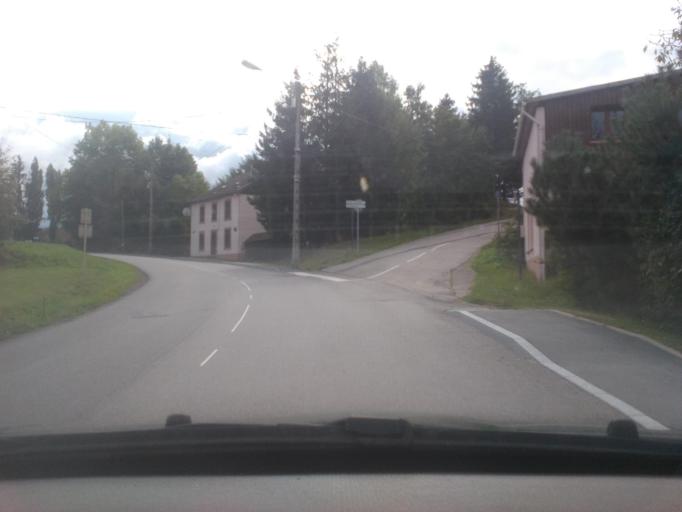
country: FR
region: Lorraine
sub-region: Departement des Vosges
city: Corcieux
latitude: 48.1708
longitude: 6.8759
